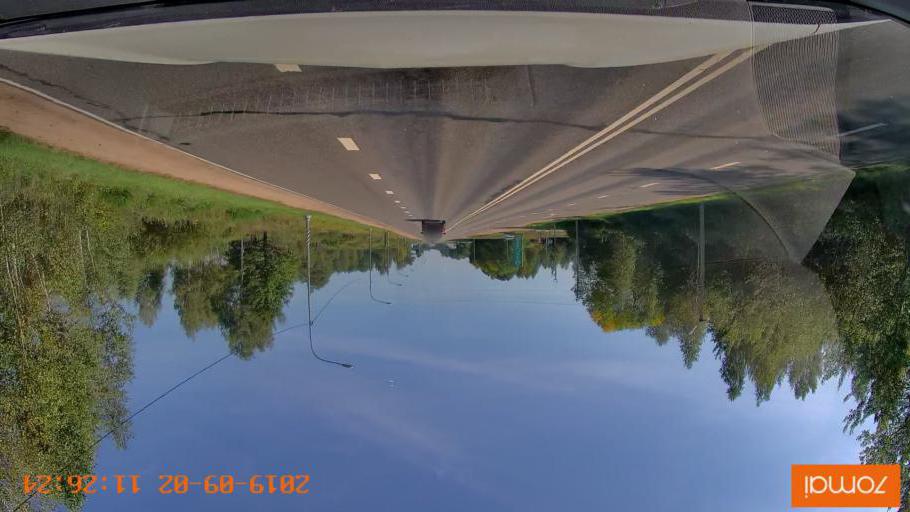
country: RU
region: Smolensk
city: Roslavl'
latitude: 53.9927
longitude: 32.9318
